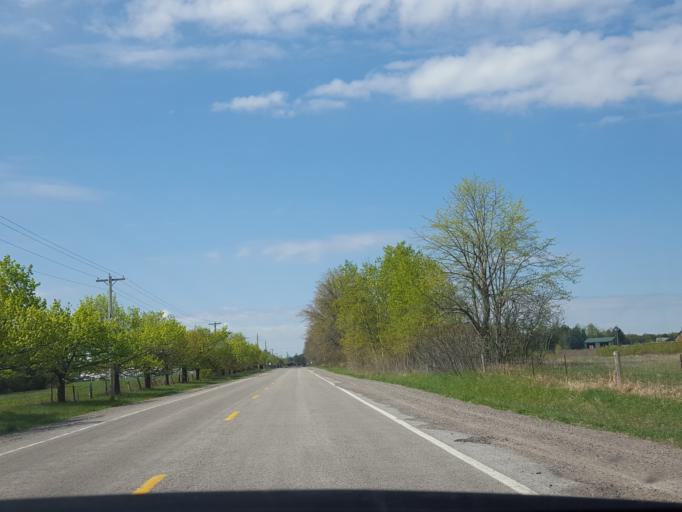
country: CA
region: Ontario
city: Uxbridge
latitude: 44.1901
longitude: -78.8838
